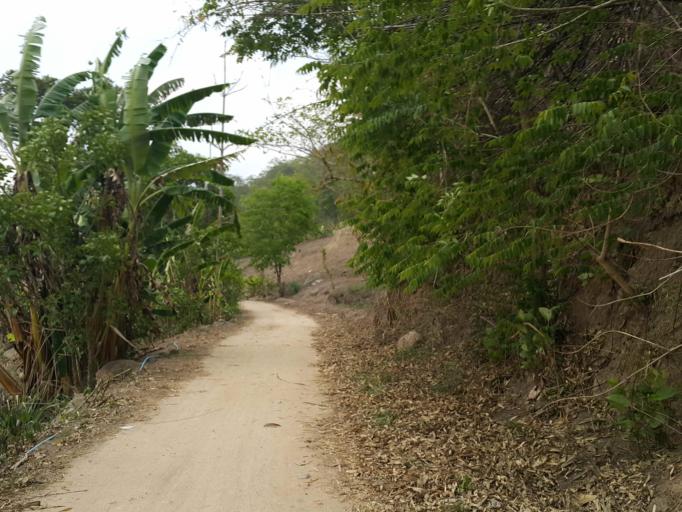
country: TH
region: Chiang Mai
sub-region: Amphoe Chiang Dao
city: Chiang Dao
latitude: 19.2758
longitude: 98.7664
